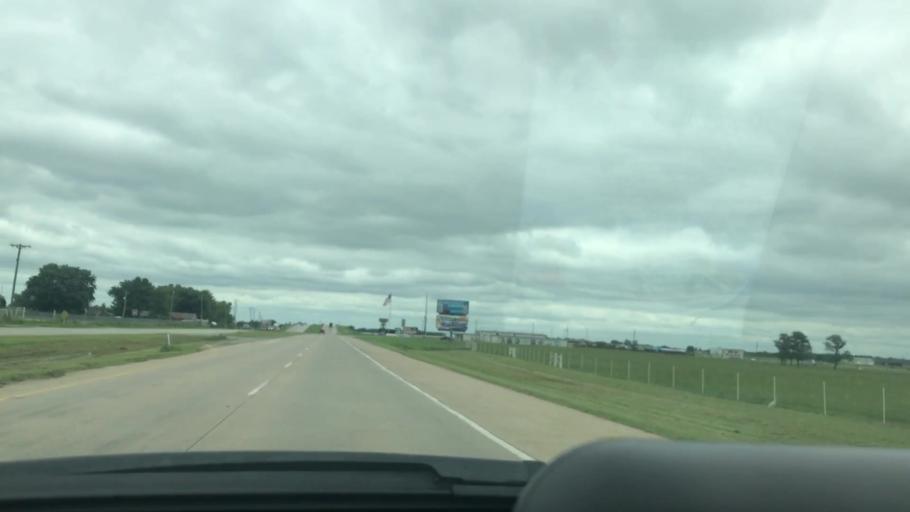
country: US
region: Oklahoma
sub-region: Craig County
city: Vinita
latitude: 36.5496
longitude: -95.2201
